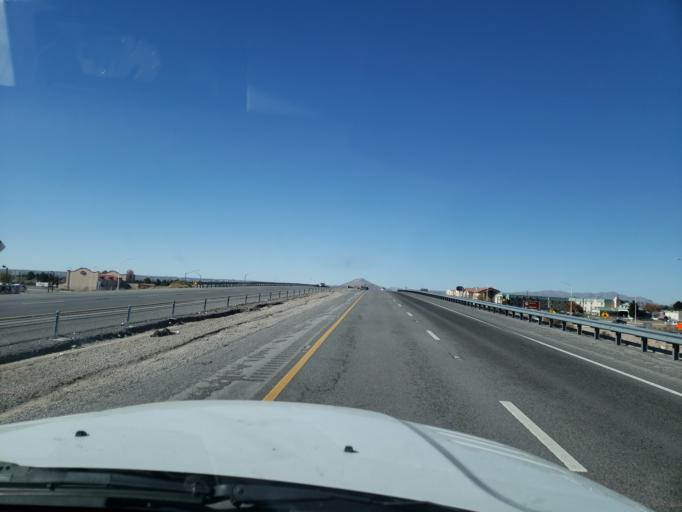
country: US
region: New Mexico
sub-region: Dona Ana County
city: Mesilla
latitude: 32.2886
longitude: -106.7884
